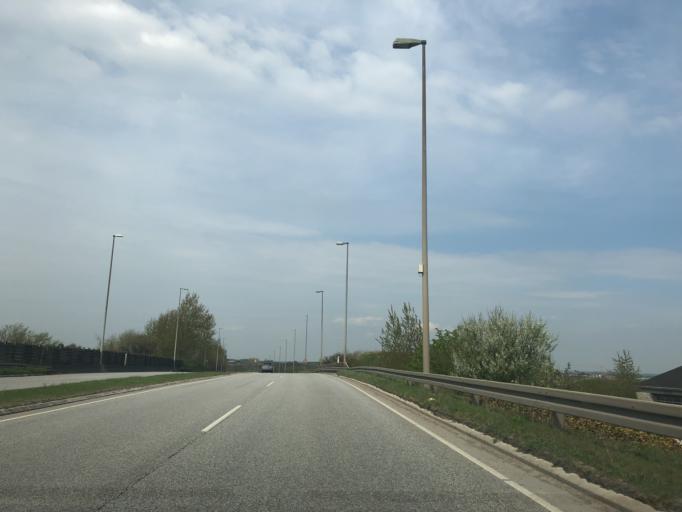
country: DK
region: Zealand
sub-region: Roskilde Kommune
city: Vindinge
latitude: 55.6462
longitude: 12.1180
